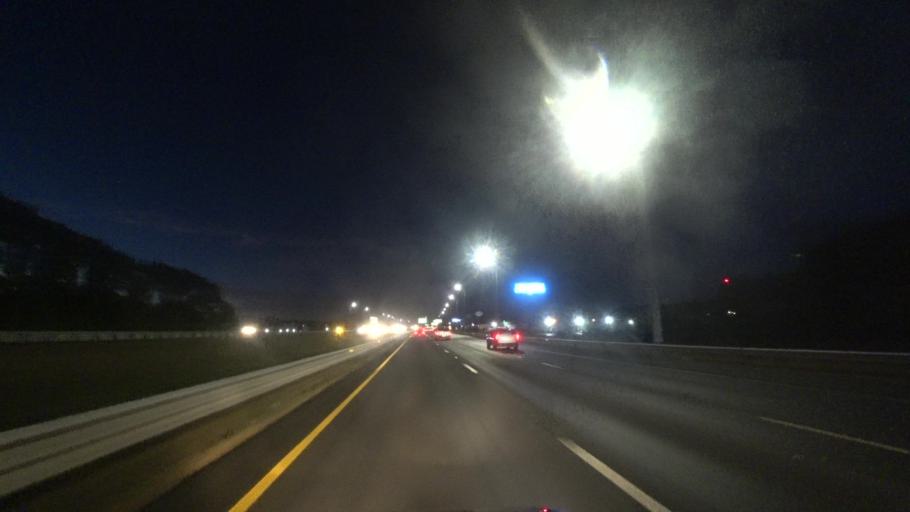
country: US
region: Massachusetts
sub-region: Essex County
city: North Andover
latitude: 42.7193
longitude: -71.1373
